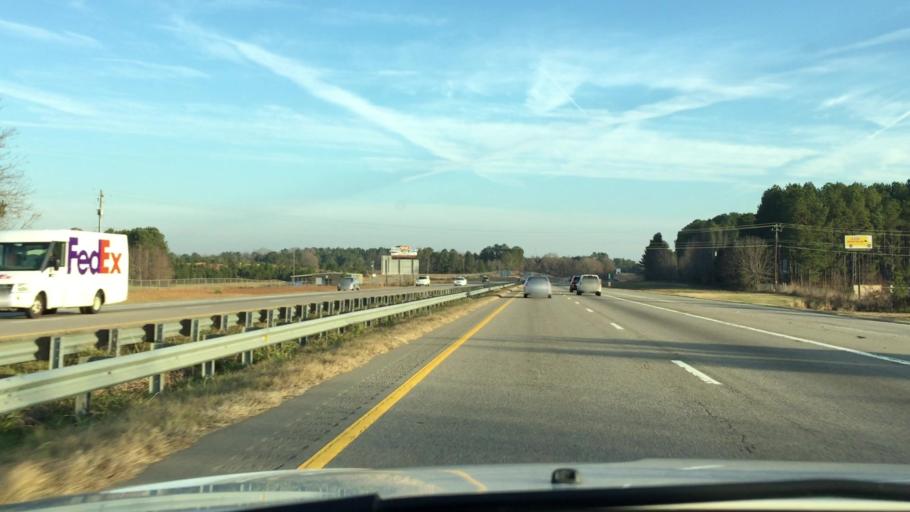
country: US
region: North Carolina
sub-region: Lee County
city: Sanford
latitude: 35.5264
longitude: -79.1827
